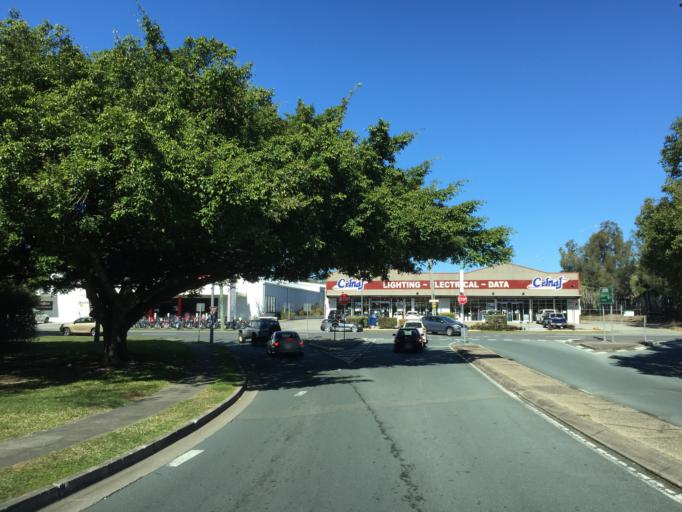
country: AU
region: Queensland
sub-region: Brisbane
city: Everton Park
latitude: -27.4187
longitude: 152.9922
